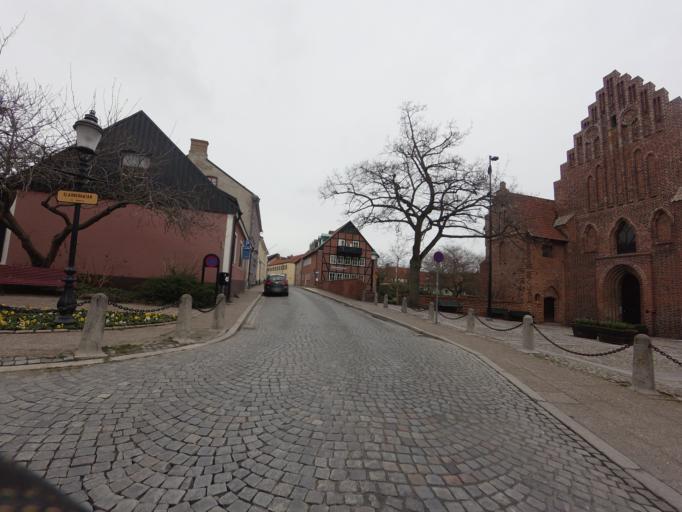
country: SE
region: Skane
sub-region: Ystads Kommun
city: Ystad
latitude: 55.4310
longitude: 13.8189
